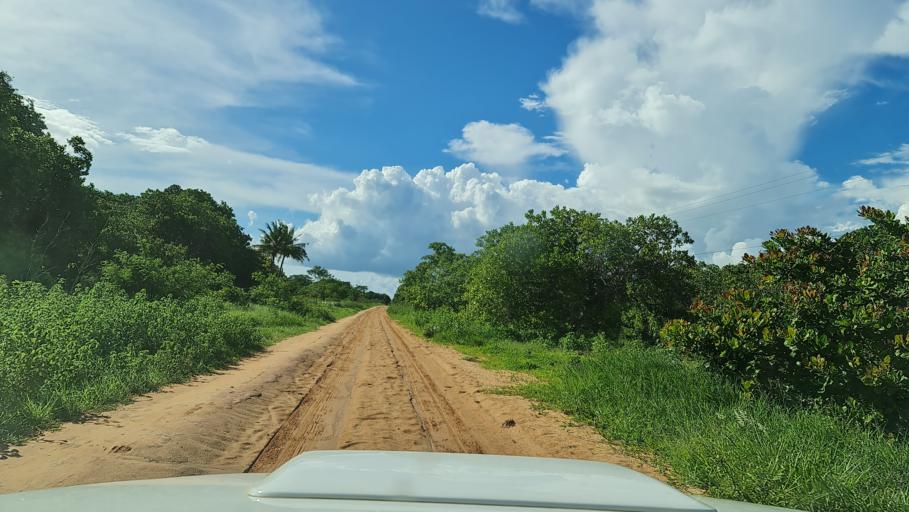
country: MZ
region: Nampula
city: Ilha de Mocambique
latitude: -15.2973
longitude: 40.1242
